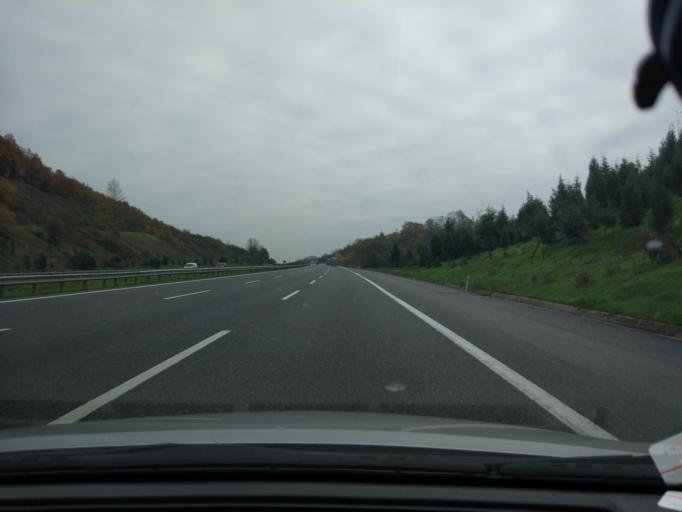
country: TR
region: Duzce
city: Gumusova
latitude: 40.8092
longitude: 30.8912
